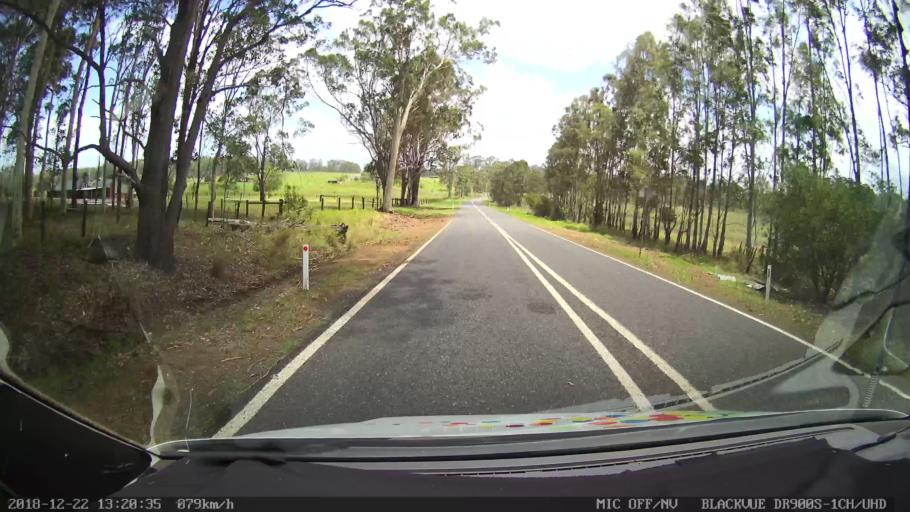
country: AU
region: New South Wales
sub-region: Clarence Valley
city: South Grafton
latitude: -29.7679
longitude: 152.9268
